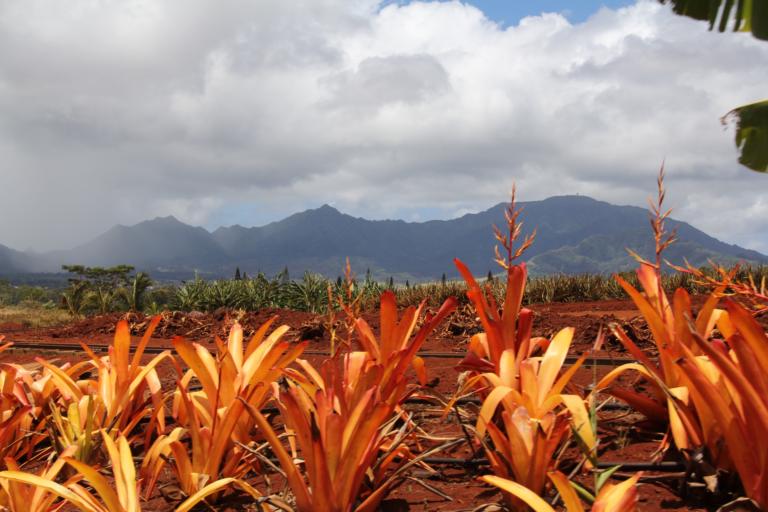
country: US
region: Hawaii
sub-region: Honolulu County
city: Whitmore Village
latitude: 21.5260
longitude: -158.0316
